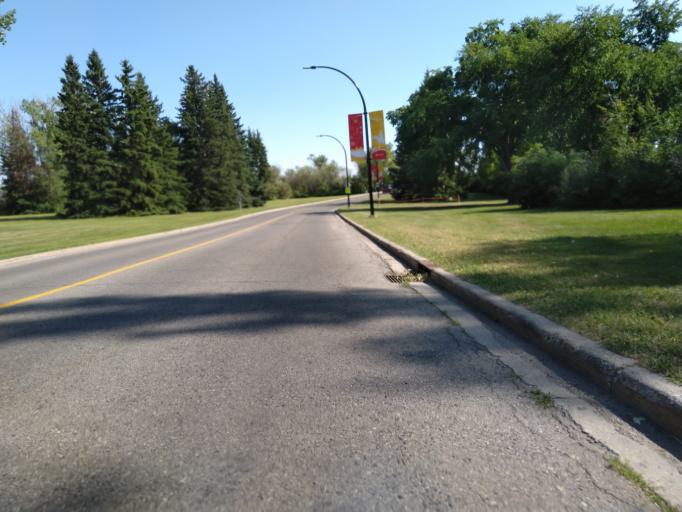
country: CA
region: Alberta
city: Calgary
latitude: 51.0784
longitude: -114.1239
